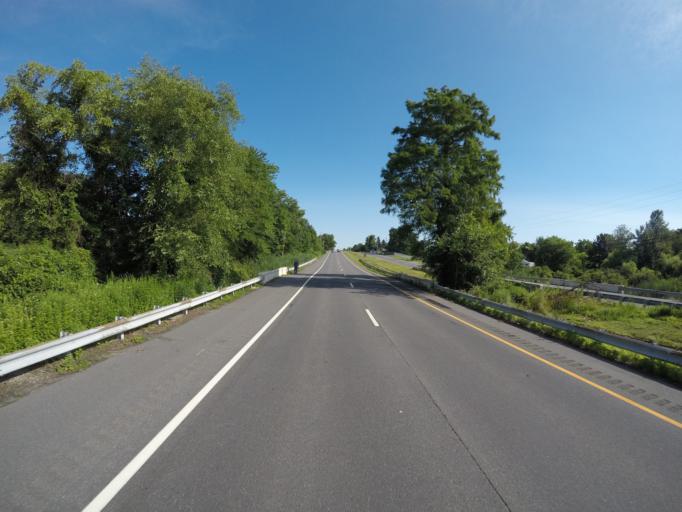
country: US
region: Delaware
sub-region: New Castle County
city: Bear
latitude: 39.5691
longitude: -75.6550
